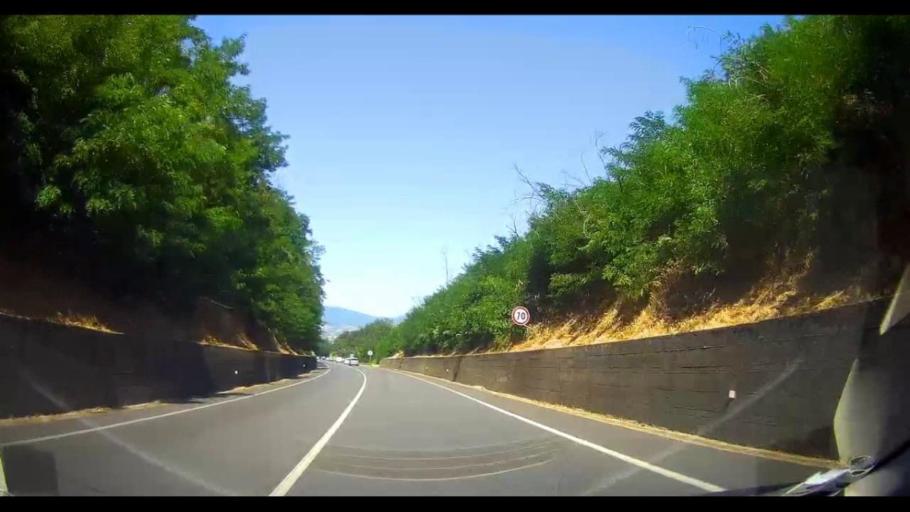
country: IT
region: Calabria
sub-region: Provincia di Cosenza
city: Zumpano
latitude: 39.2980
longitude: 16.2999
